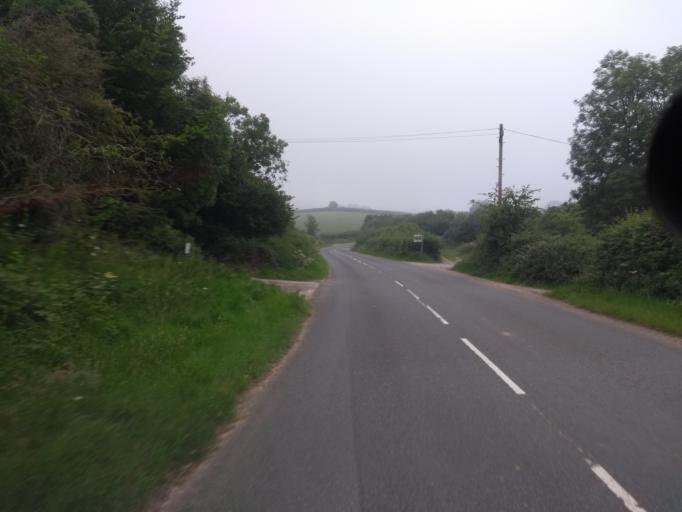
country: GB
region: England
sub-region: Somerset
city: Crewkerne
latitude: 50.8326
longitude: -2.8121
